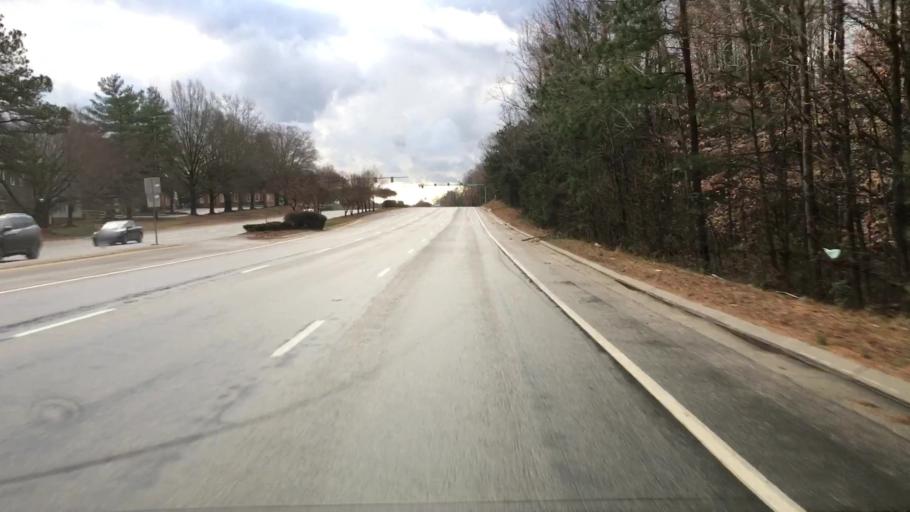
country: US
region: Virginia
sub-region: Chesterfield County
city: Bon Air
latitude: 37.5009
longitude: -77.6094
